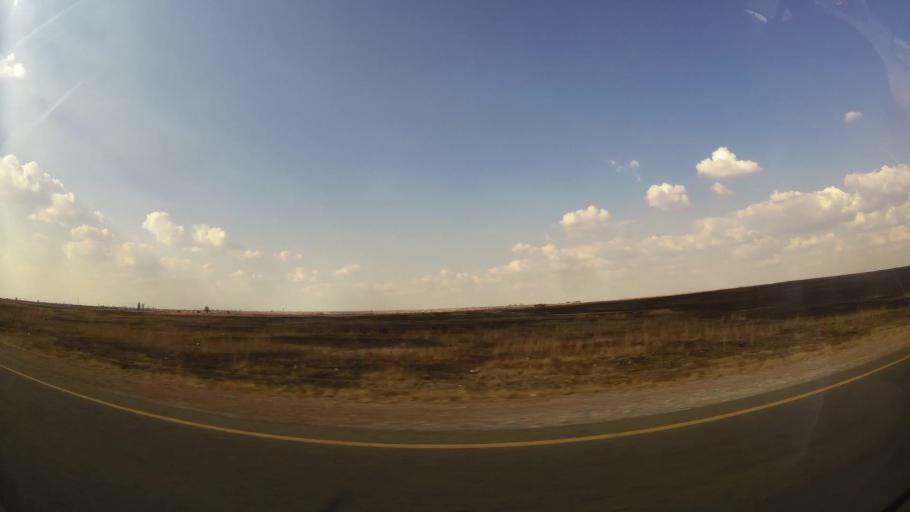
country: ZA
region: Gauteng
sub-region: Sedibeng District Municipality
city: Heidelberg
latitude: -26.3855
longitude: 28.3450
